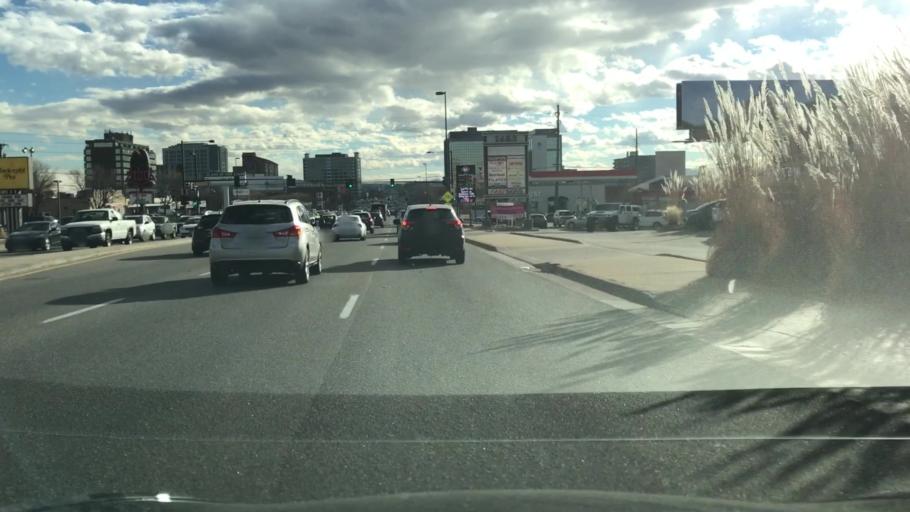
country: US
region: Colorado
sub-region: Arapahoe County
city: Glendale
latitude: 39.6905
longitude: -104.9408
